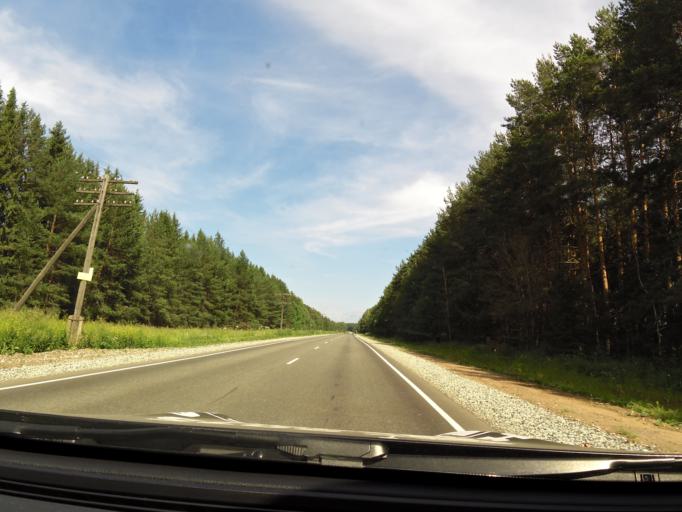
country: RU
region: Kirov
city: Slobodskoy
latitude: 58.7801
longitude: 50.4572
